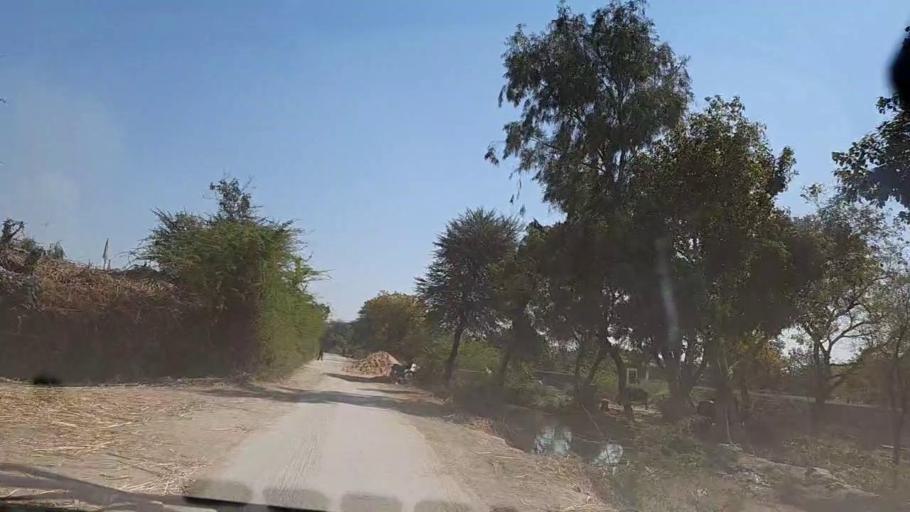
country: PK
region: Sindh
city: Mirpur Khas
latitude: 25.4314
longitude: 69.0201
